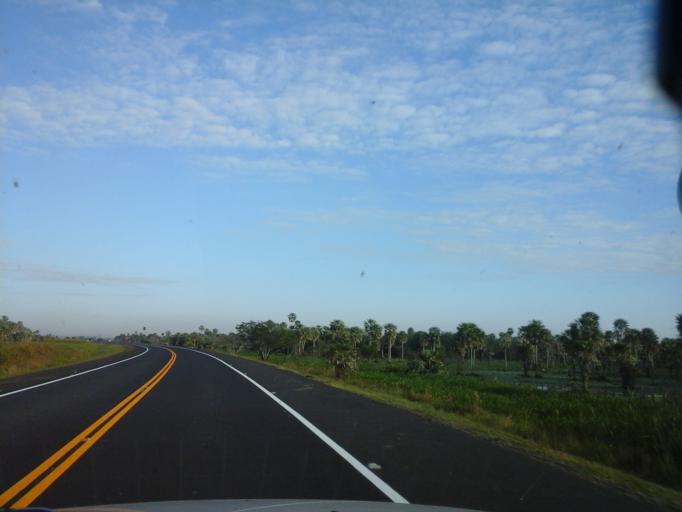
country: PY
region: Neembucu
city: Cerrito
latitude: -26.8681
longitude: -57.7613
